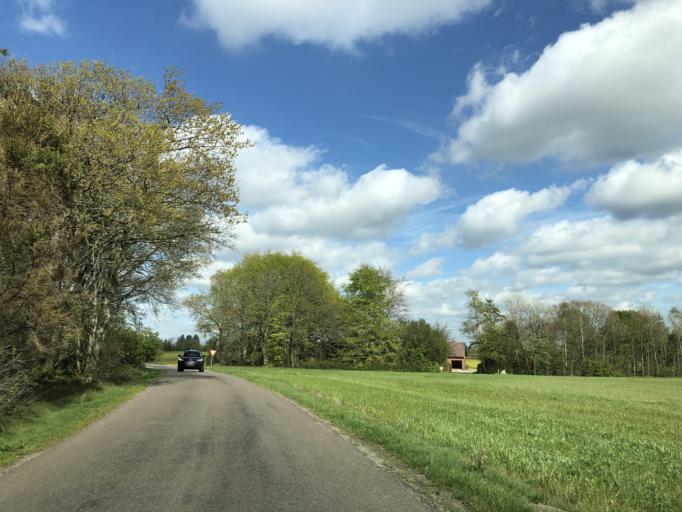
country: DK
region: Central Jutland
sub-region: Herning Kommune
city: Avlum
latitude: 56.3052
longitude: 8.7379
